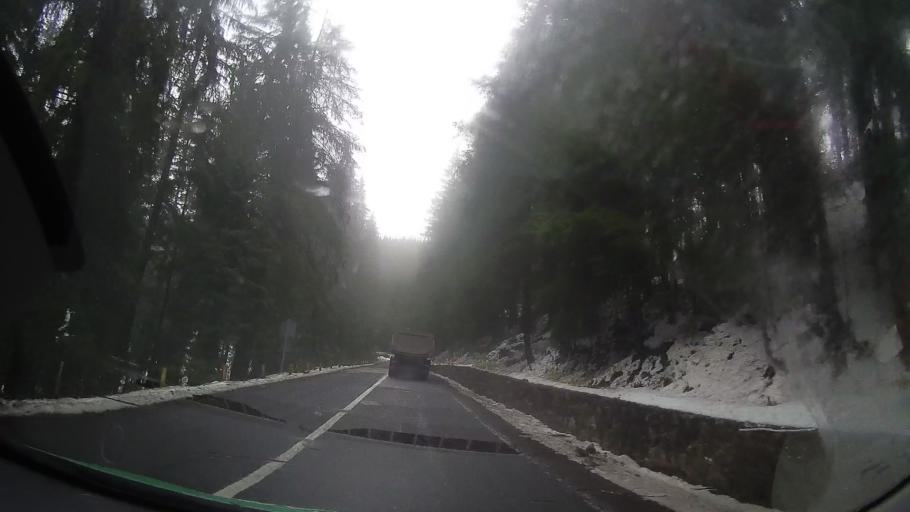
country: RO
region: Harghita
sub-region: Municipiul Gheorgheni
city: Gheorgheni
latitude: 46.7776
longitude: 25.7288
